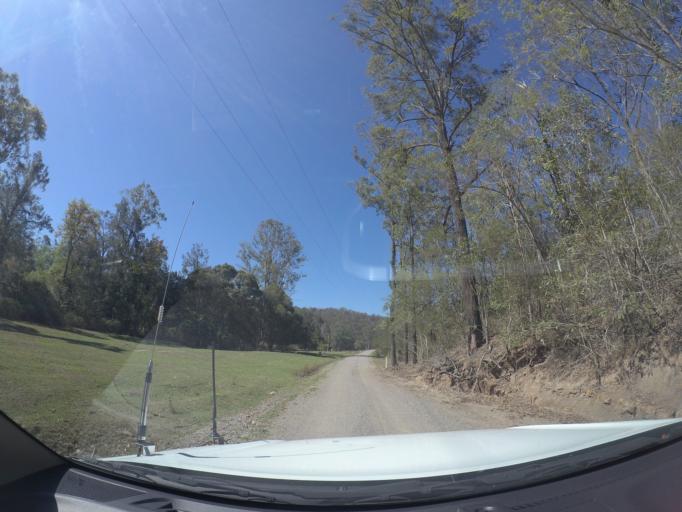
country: AU
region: Queensland
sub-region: Ipswich
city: Springfield Lakes
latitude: -27.7520
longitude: 152.8931
